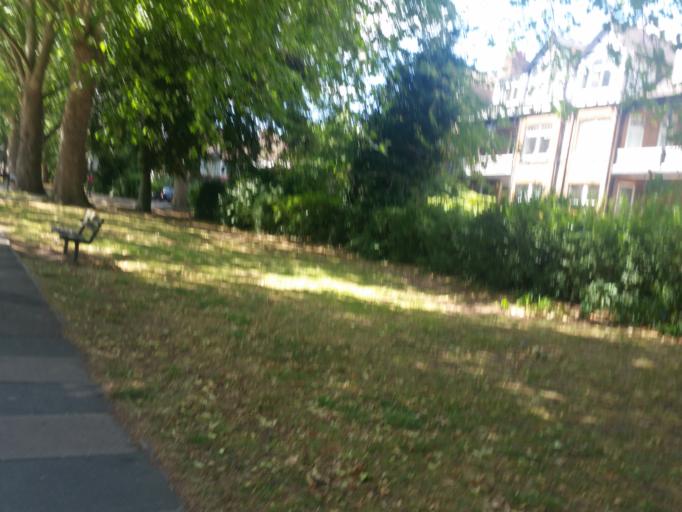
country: GB
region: England
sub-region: Greater London
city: Crouch End
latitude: 51.5868
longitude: -0.1269
